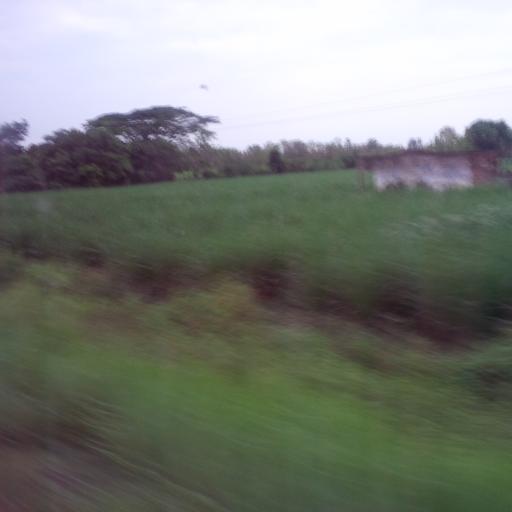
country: EC
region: Canar
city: La Troncal
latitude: -2.3427
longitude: -79.3755
